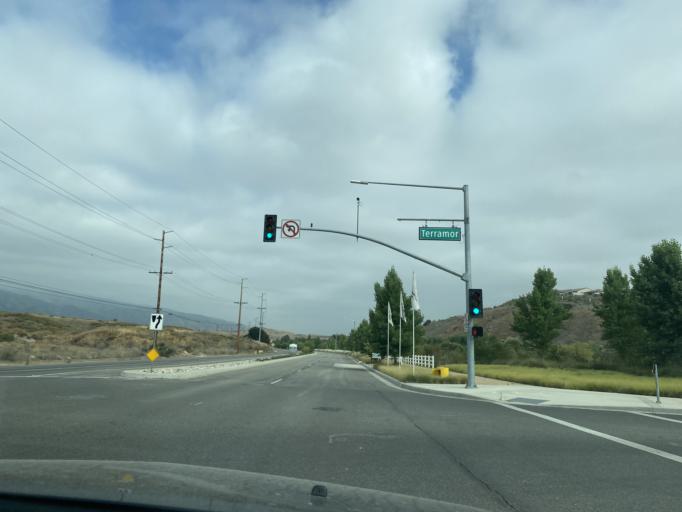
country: US
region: California
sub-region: Riverside County
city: El Cerrito
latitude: 33.7598
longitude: -117.4599
